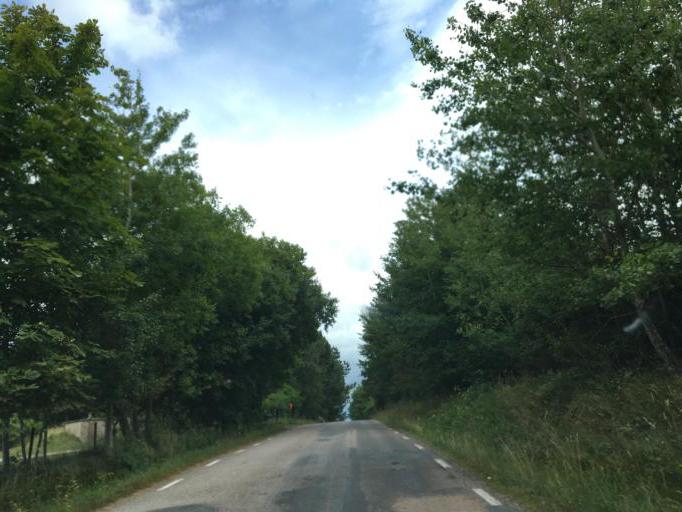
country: SE
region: Vaestra Goetaland
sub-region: Sotenas Kommun
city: Hunnebostrand
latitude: 58.4115
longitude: 11.2667
